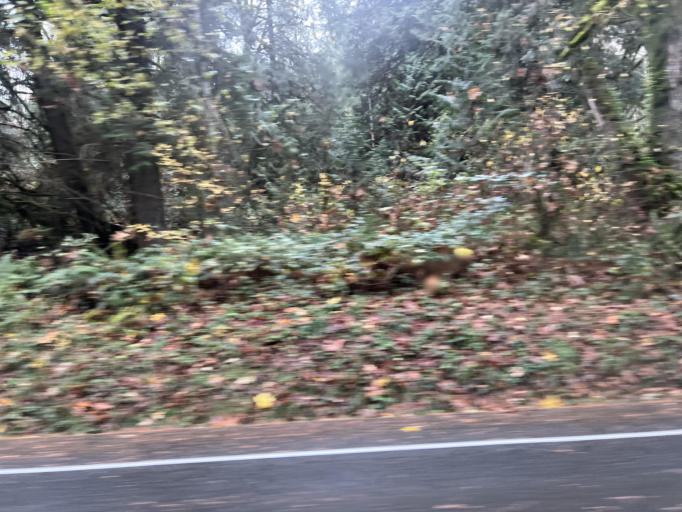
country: US
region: Washington
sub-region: King County
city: Fall City
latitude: 47.5387
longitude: -121.9105
